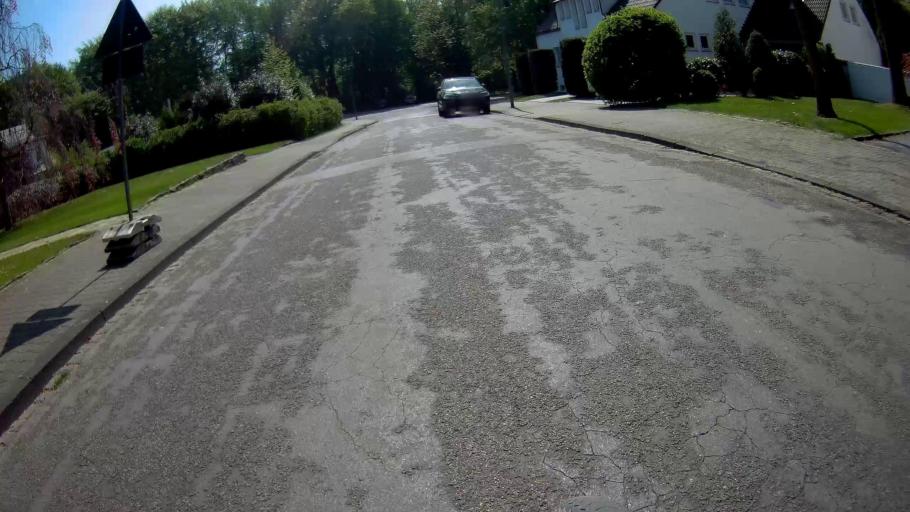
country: DE
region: North Rhine-Westphalia
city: Herten
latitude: 51.5708
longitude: 7.0740
